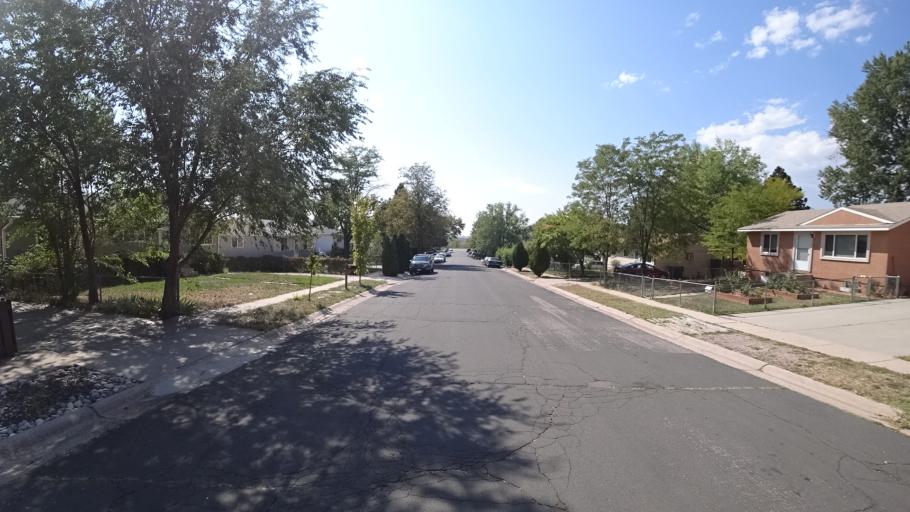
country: US
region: Colorado
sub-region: El Paso County
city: Colorado Springs
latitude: 38.8193
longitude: -104.7909
